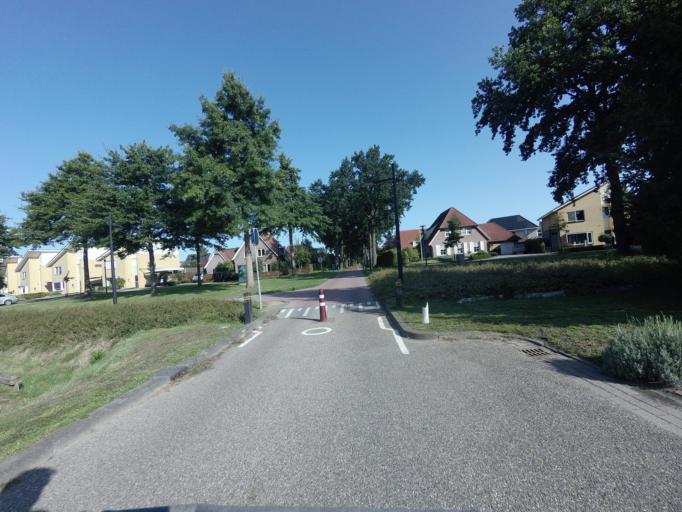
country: NL
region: Overijssel
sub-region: Gemeente Raalte
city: Raalte
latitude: 52.3960
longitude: 6.2845
